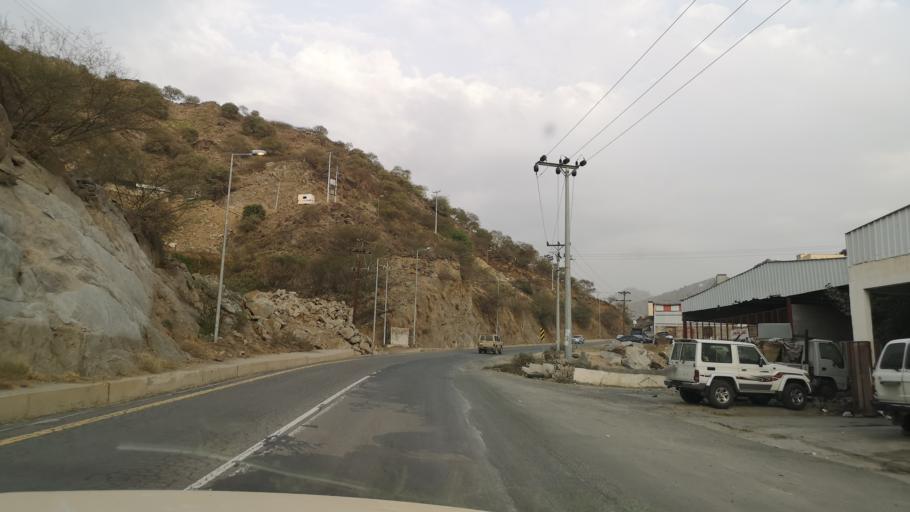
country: YE
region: Sa'dah
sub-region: Monabbih
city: Suq al Khamis
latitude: 17.3490
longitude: 43.1386
